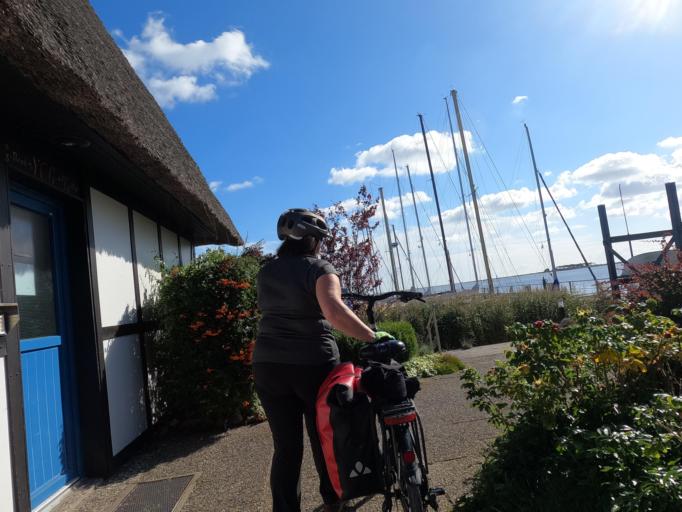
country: DE
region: Schleswig-Holstein
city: Grossenbrode
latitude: 54.3561
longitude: 11.0604
